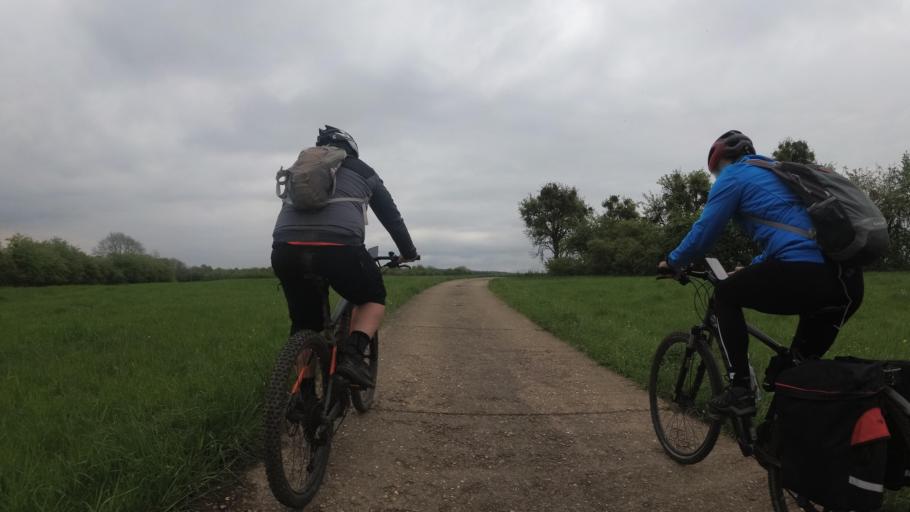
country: FR
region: Lorraine
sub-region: Departement de la Moselle
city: Bouzonville
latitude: 49.3453
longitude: 6.5989
